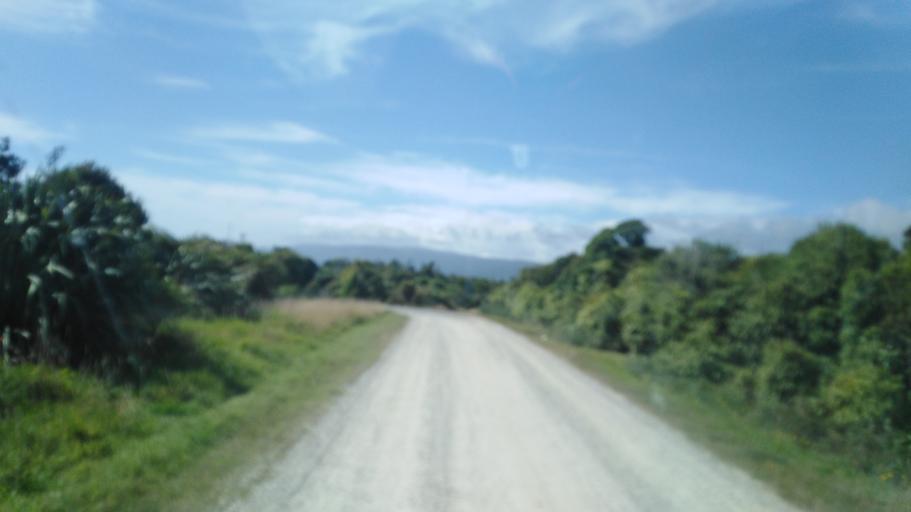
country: NZ
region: West Coast
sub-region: Buller District
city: Westport
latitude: -41.2626
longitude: 172.1144
